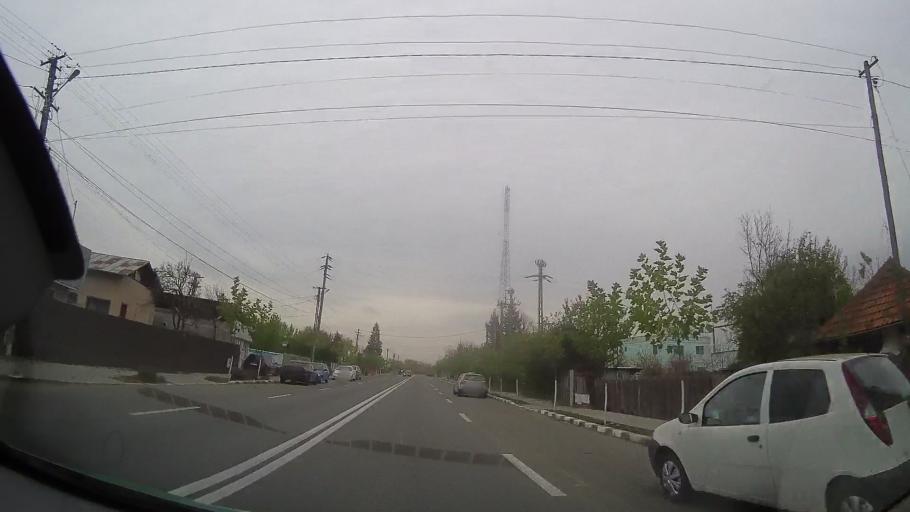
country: RO
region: Prahova
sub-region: Oras Urlati
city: Urlati
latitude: 44.9724
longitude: 26.2334
